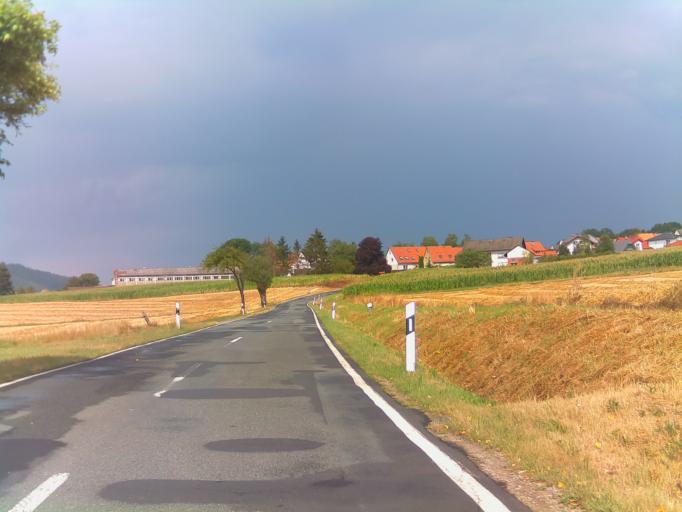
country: DE
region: Hesse
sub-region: Regierungsbezirk Kassel
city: Niederaula
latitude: 50.7895
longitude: 9.6117
